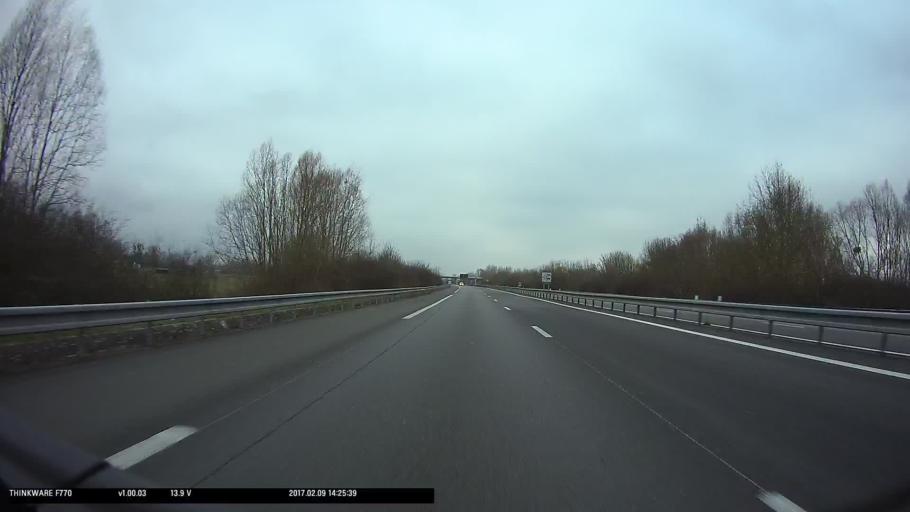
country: FR
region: Centre
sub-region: Departement du Cher
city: Foecy
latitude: 47.1837
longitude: 2.1712
